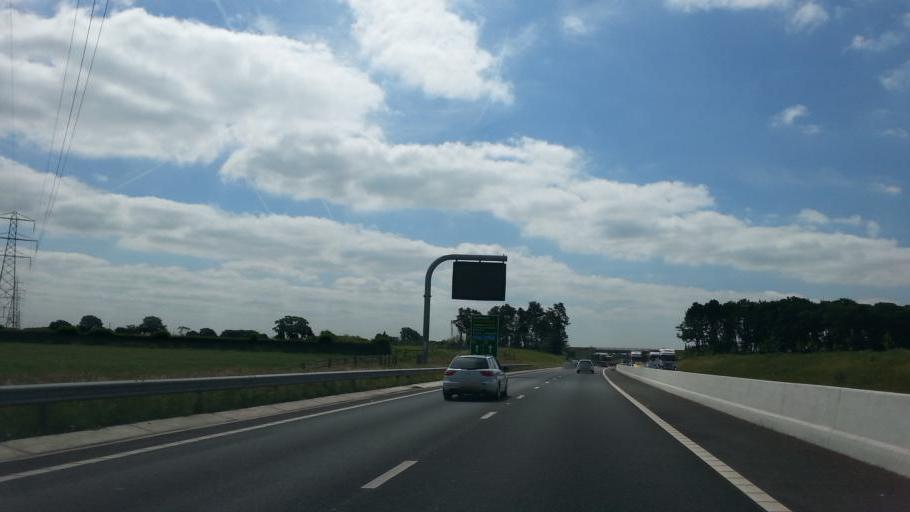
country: GB
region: England
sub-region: Cheshire East
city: Mere
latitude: 53.3233
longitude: -2.4209
